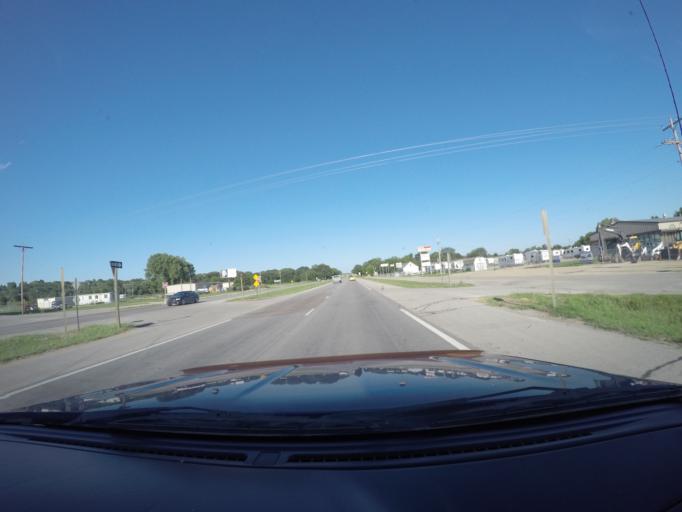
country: US
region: Kansas
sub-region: Shawnee County
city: Topeka
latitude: 39.0910
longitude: -95.6440
